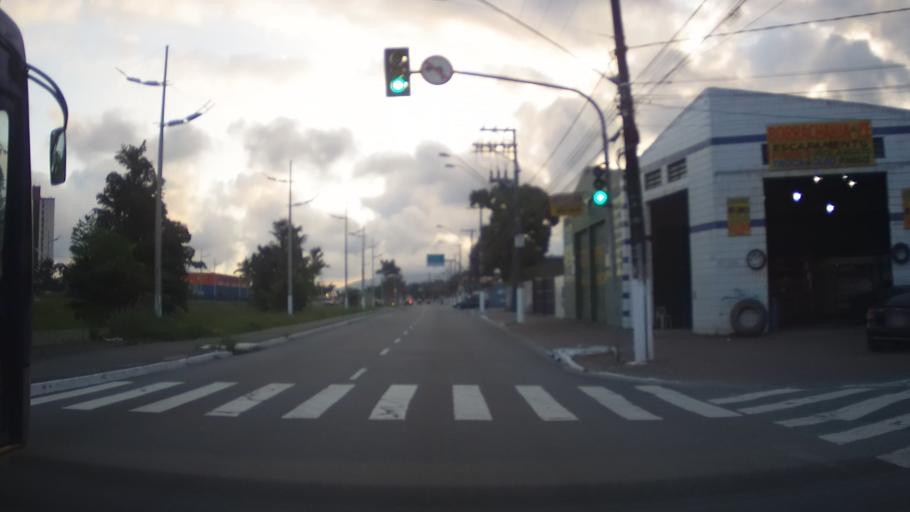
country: BR
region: Sao Paulo
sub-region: Praia Grande
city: Praia Grande
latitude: -24.0253
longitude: -46.4940
